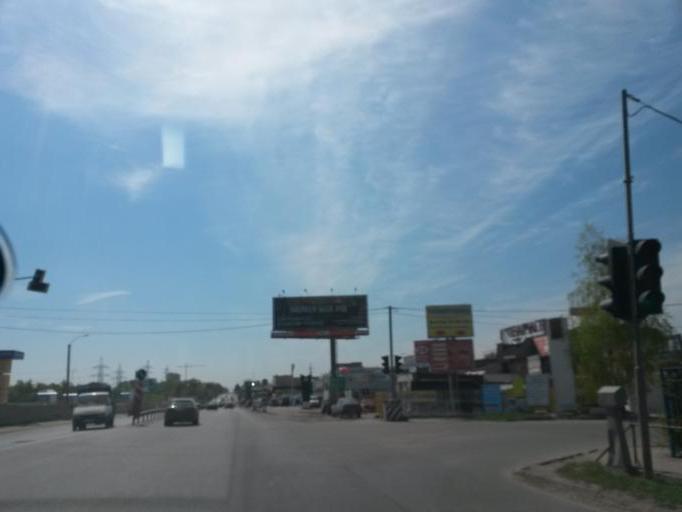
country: RU
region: Moskovskaya
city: Shcherbinka
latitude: 55.4944
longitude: 37.5693
